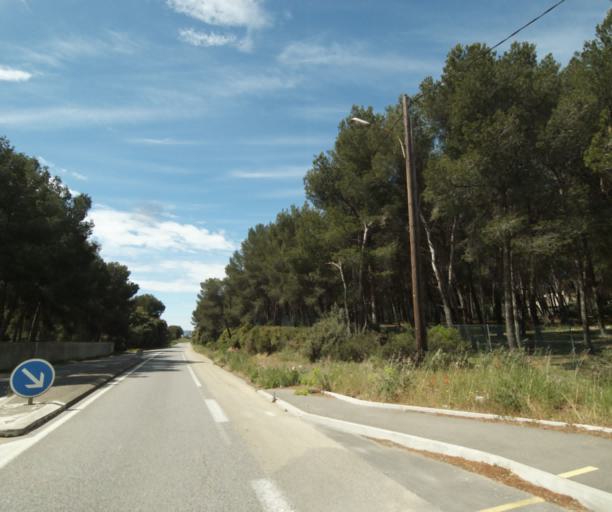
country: FR
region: Provence-Alpes-Cote d'Azur
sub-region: Departement des Bouches-du-Rhone
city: Rognac
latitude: 43.5088
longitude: 5.2249
